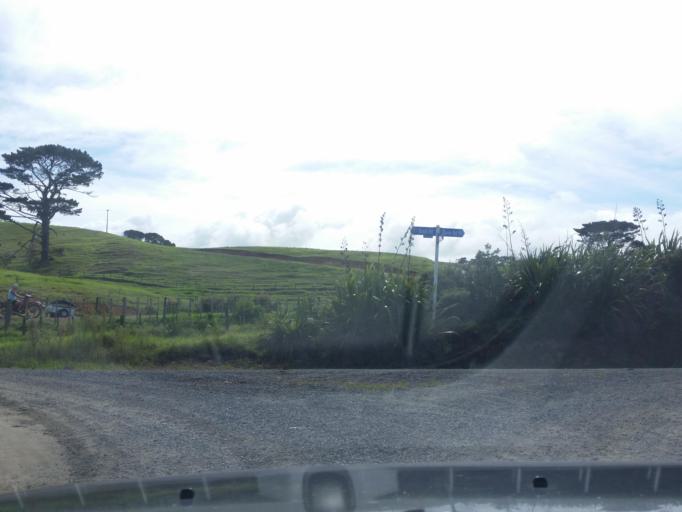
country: NZ
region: Northland
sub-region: Kaipara District
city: Dargaville
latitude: -35.9195
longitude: 173.7367
